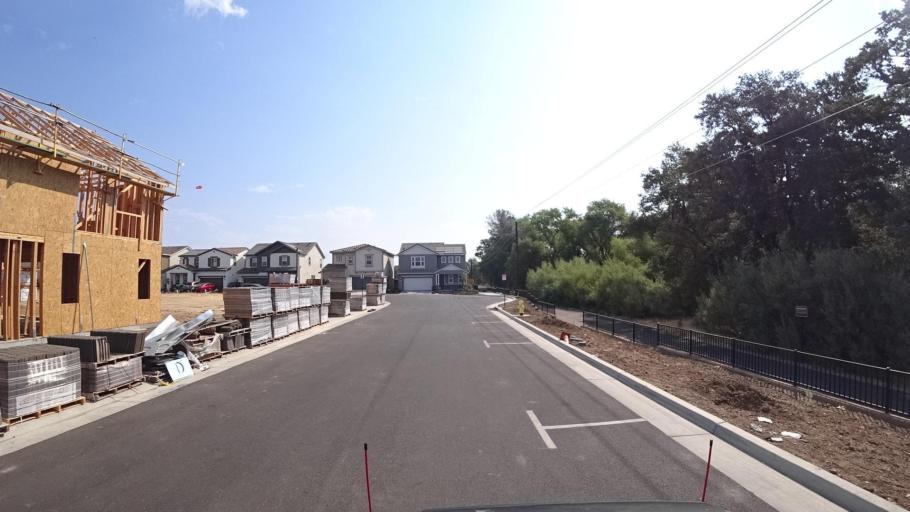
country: US
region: California
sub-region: Placer County
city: Rocklin
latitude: 38.7999
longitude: -121.2182
